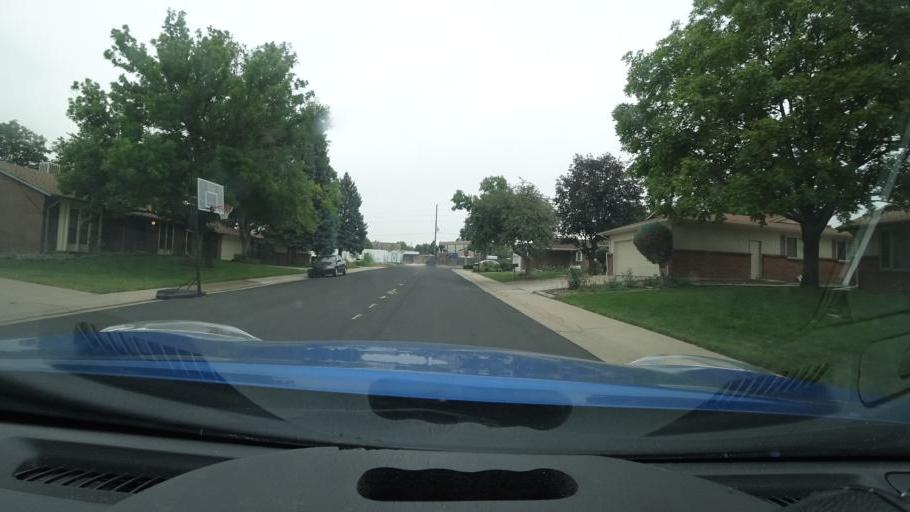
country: US
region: Colorado
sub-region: Arapahoe County
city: Glendale
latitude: 39.6810
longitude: -104.9063
